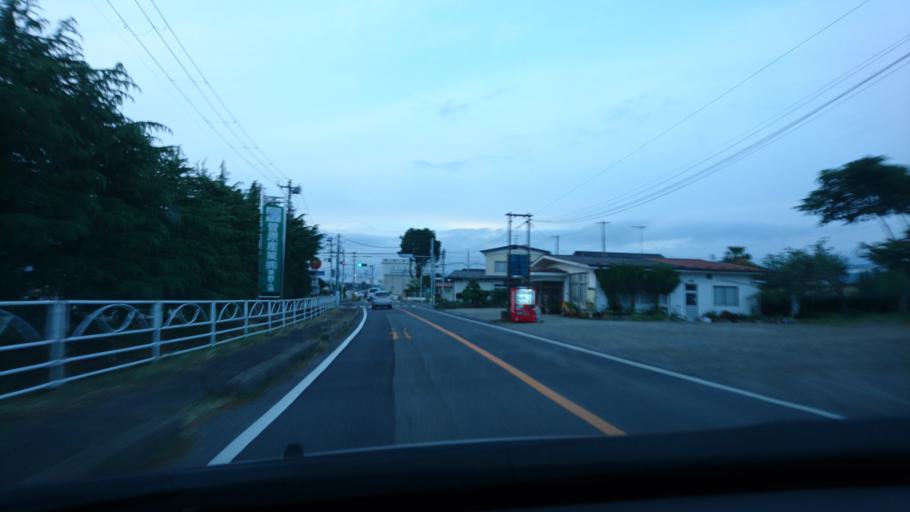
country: JP
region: Iwate
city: Ichinoseki
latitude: 38.7994
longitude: 140.9799
